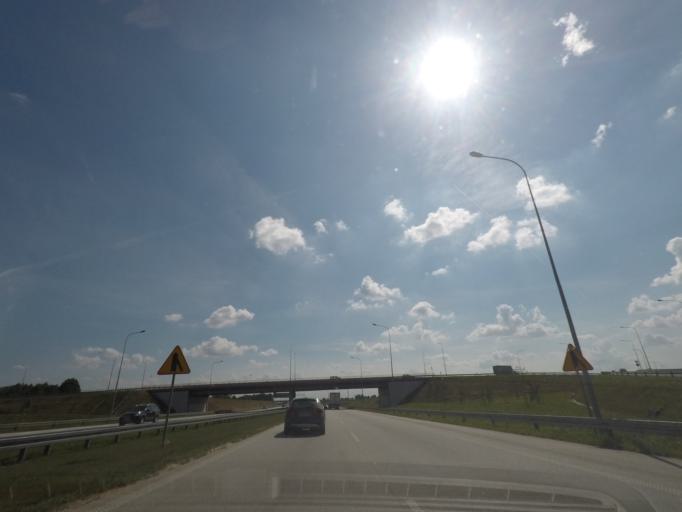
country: PL
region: Lodz Voivodeship
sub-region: Powiat lodzki wschodni
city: Andrespol
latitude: 51.7982
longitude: 19.6206
